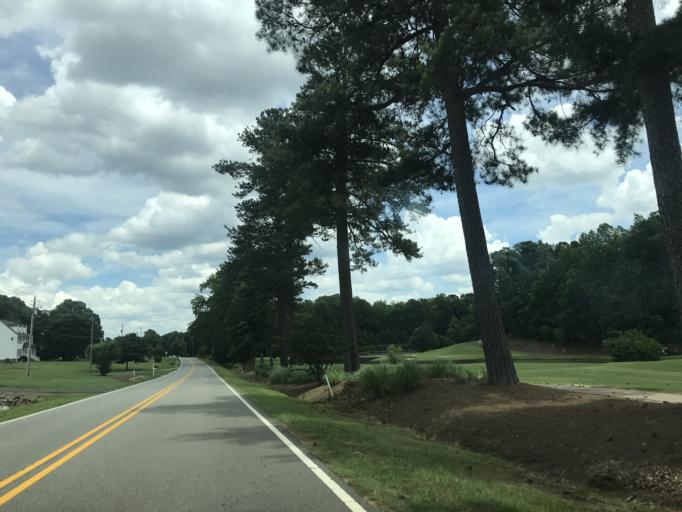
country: US
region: North Carolina
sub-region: Wake County
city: West Raleigh
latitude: 35.9135
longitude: -78.6880
